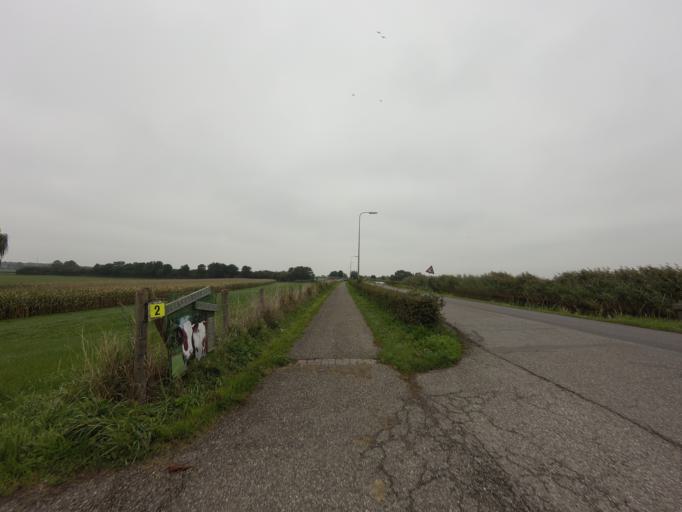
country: NL
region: South Holland
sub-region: Gemeente Nieuwkoop
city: Nieuwkoop
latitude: 52.1963
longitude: 4.7723
